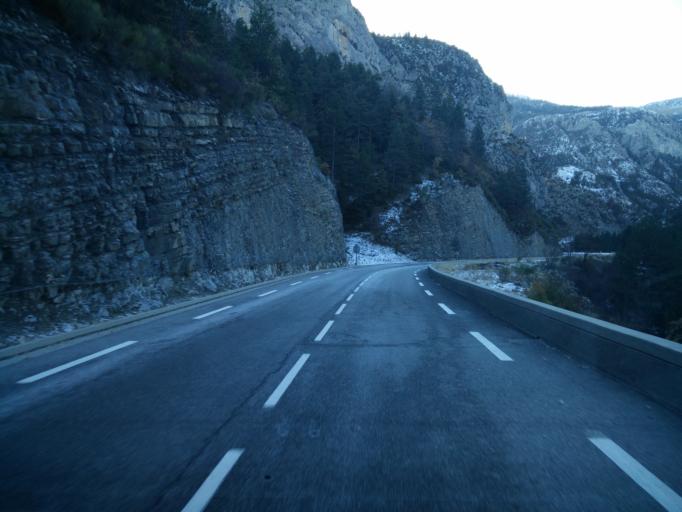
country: FR
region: Provence-Alpes-Cote d'Azur
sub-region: Departement des Alpes-de-Haute-Provence
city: Annot
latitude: 43.9471
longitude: 6.6894
